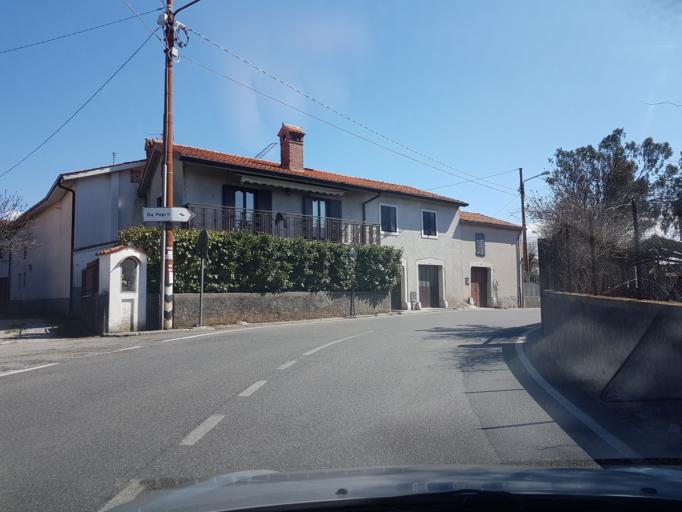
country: IT
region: Friuli Venezia Giulia
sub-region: Provincia di Trieste
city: Dolina
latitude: 45.6445
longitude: 13.8627
